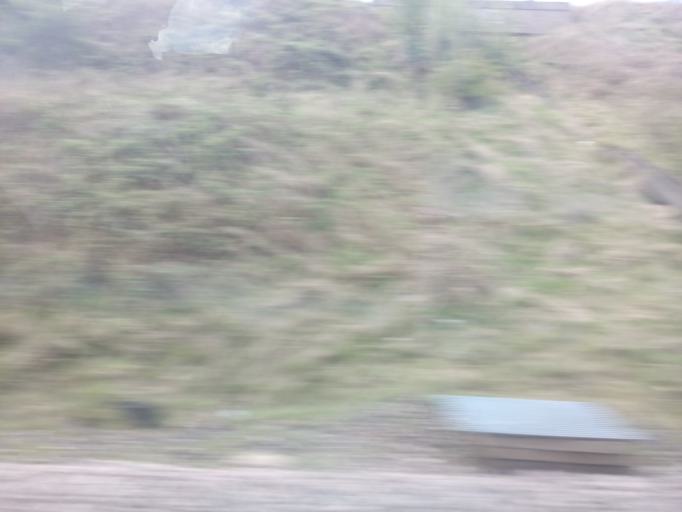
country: GB
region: England
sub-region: County Durham
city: Durham
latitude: 54.7987
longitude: -1.5614
